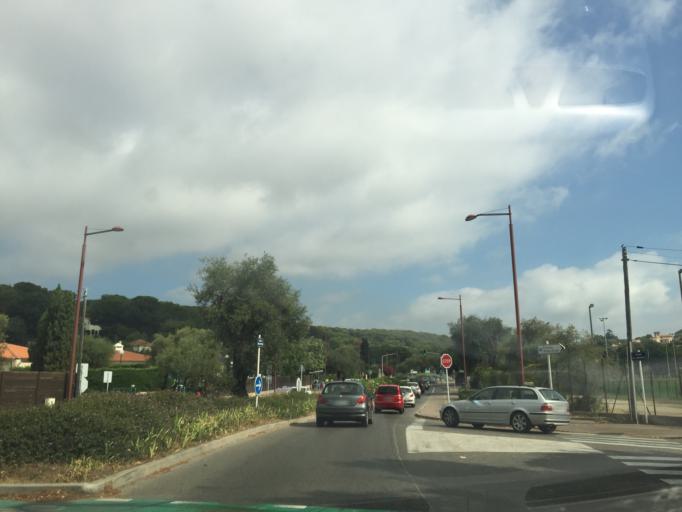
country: FR
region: Provence-Alpes-Cote d'Azur
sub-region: Departement des Alpes-Maritimes
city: Vallauris
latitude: 43.5796
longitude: 7.0899
